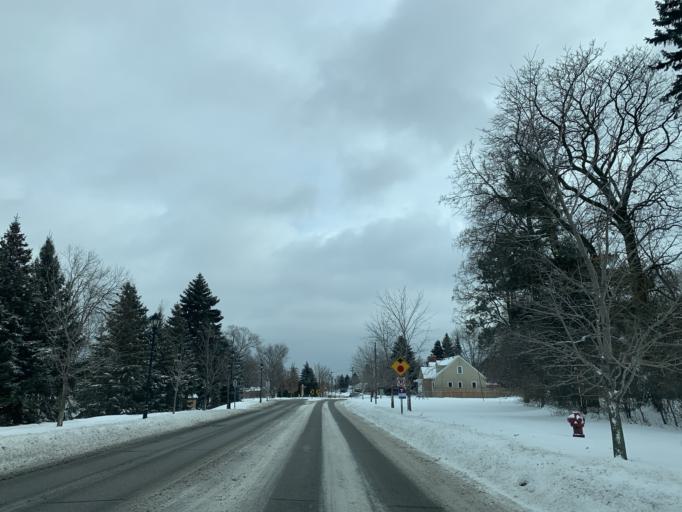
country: US
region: Minnesota
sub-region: Ramsey County
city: Little Canada
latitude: 45.0246
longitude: -93.0957
